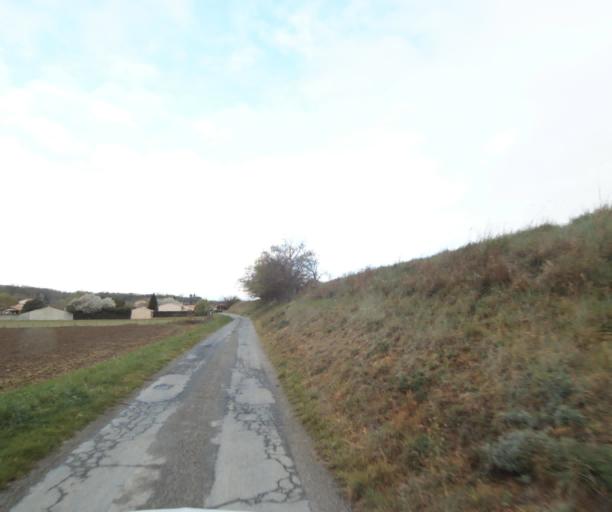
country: FR
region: Midi-Pyrenees
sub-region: Departement de l'Ariege
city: Saverdun
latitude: 43.2272
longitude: 1.5920
